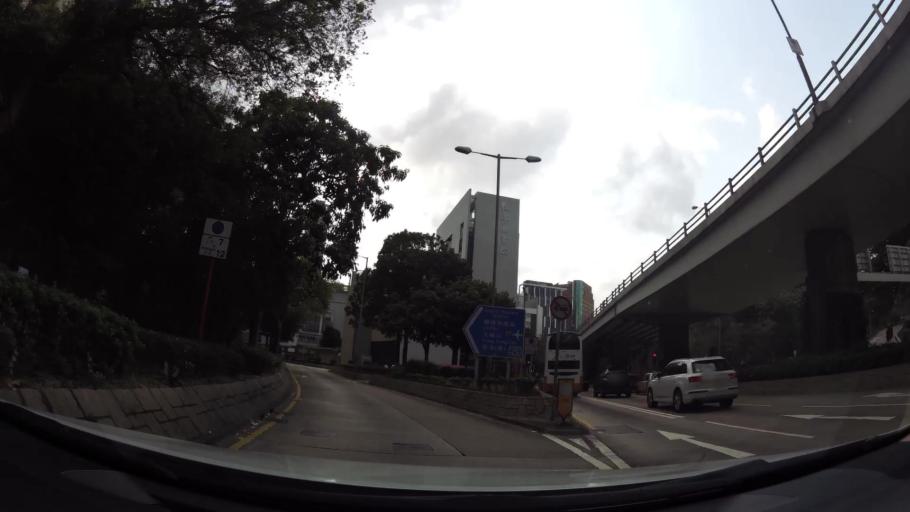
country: HK
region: Kowloon City
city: Kowloon
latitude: 22.3068
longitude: 114.1748
